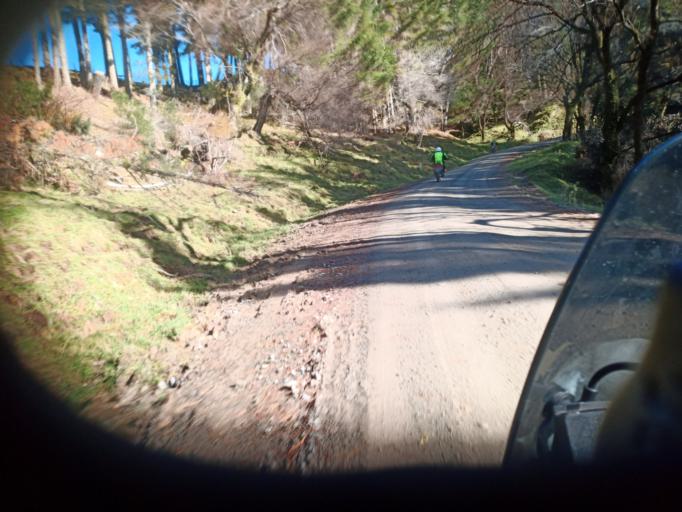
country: NZ
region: Gisborne
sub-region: Gisborne District
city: Gisborne
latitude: -38.0977
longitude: 178.1057
